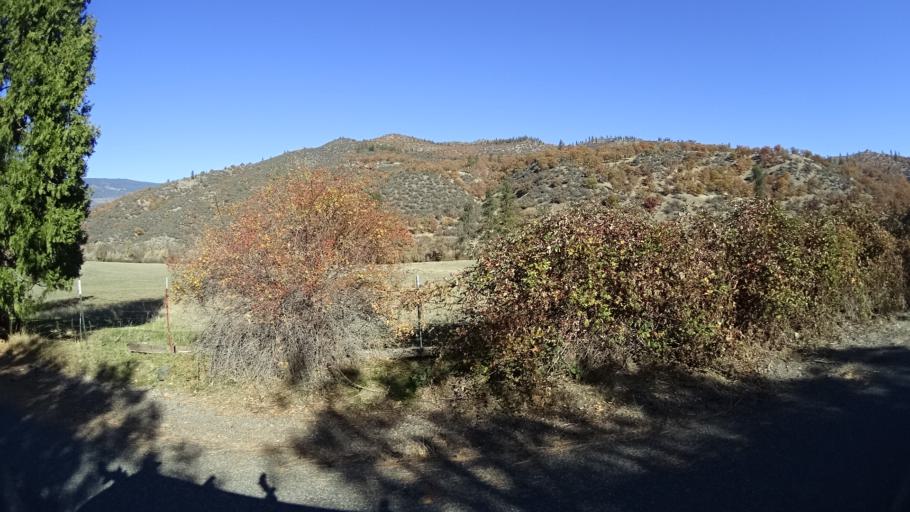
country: US
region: California
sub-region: Siskiyou County
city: Yreka
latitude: 41.8347
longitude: -122.8578
